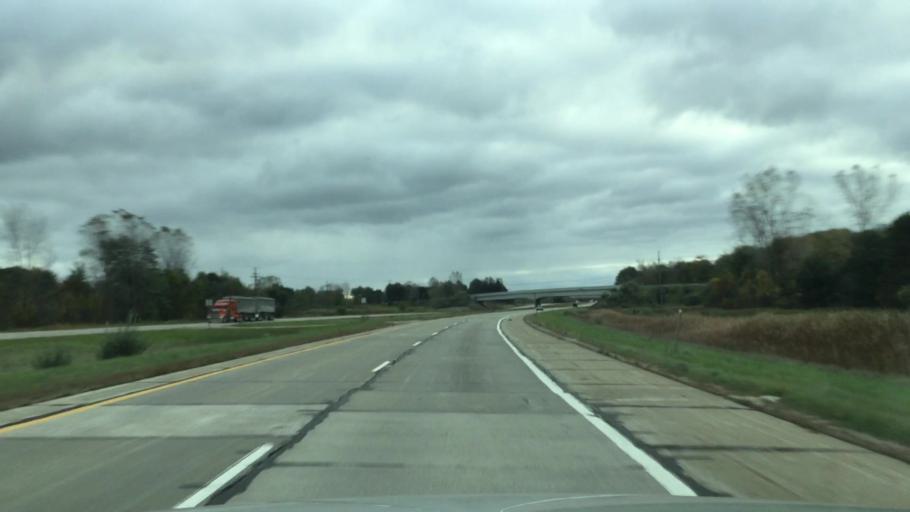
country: US
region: Michigan
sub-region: Saint Clair County
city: Capac
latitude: 42.9861
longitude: -82.8573
